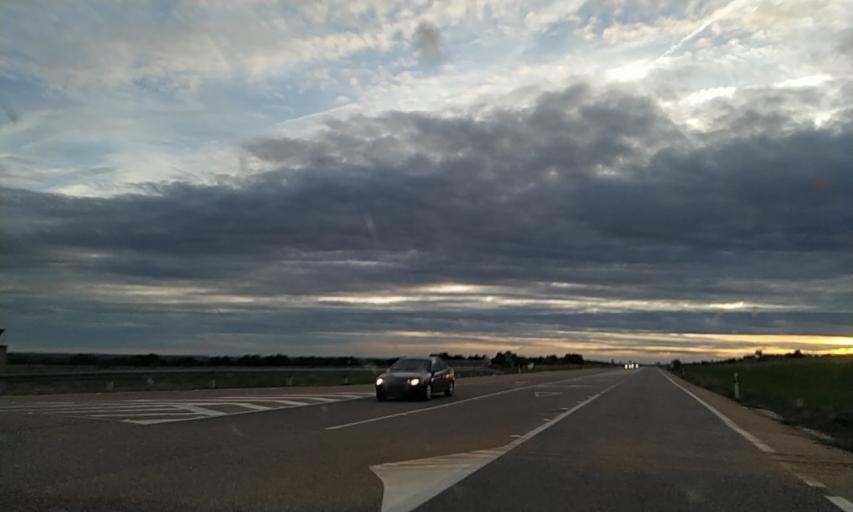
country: ES
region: Extremadura
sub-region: Provincia de Badajoz
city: La Roca de la Sierra
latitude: 39.1089
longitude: -6.7000
